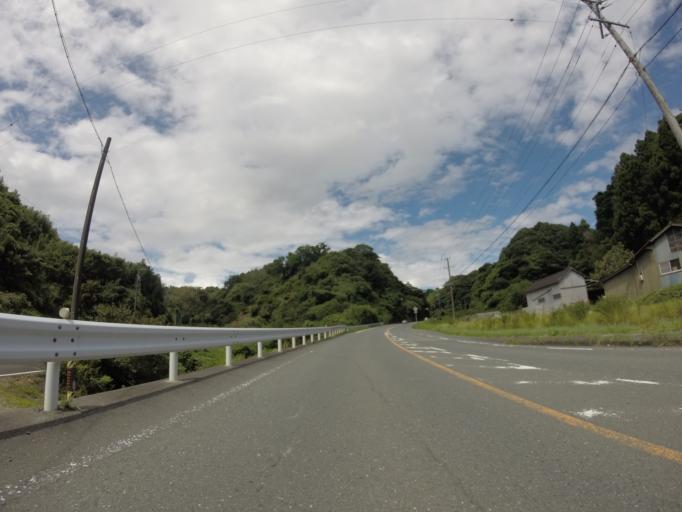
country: JP
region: Shizuoka
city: Kakegawa
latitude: 34.7353
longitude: 138.0403
